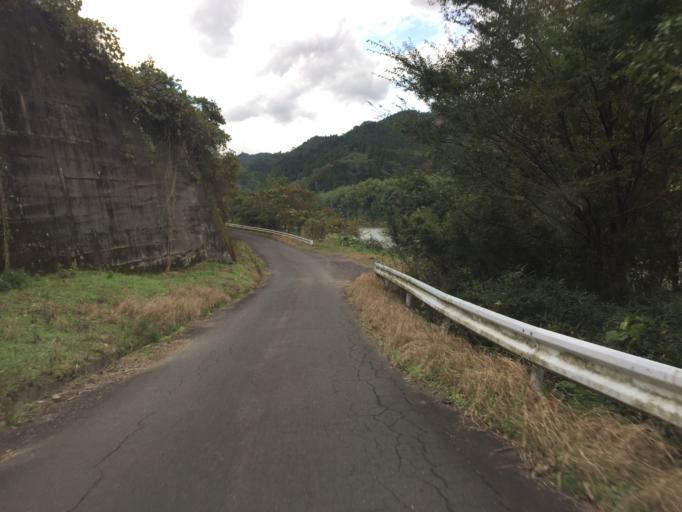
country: JP
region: Miyagi
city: Marumori
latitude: 37.9323
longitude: 140.7188
